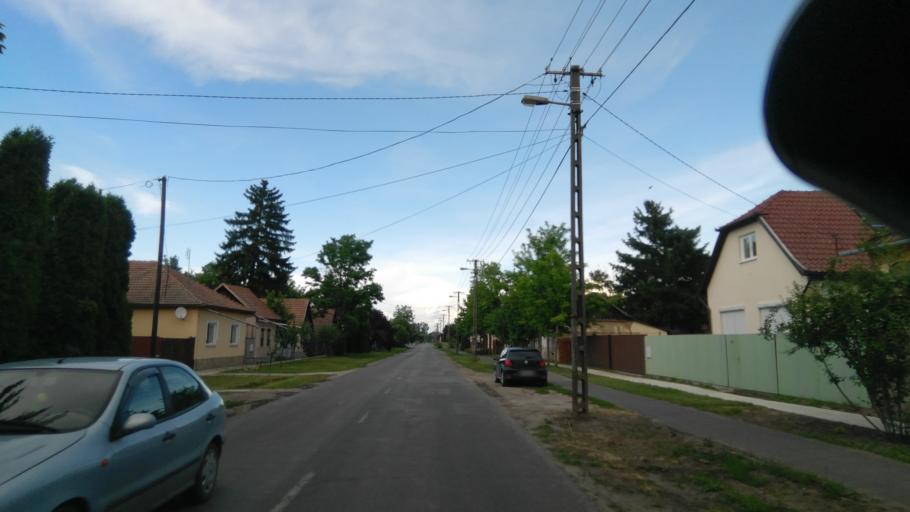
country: HU
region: Bekes
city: Kevermes
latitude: 46.4195
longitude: 21.1879
